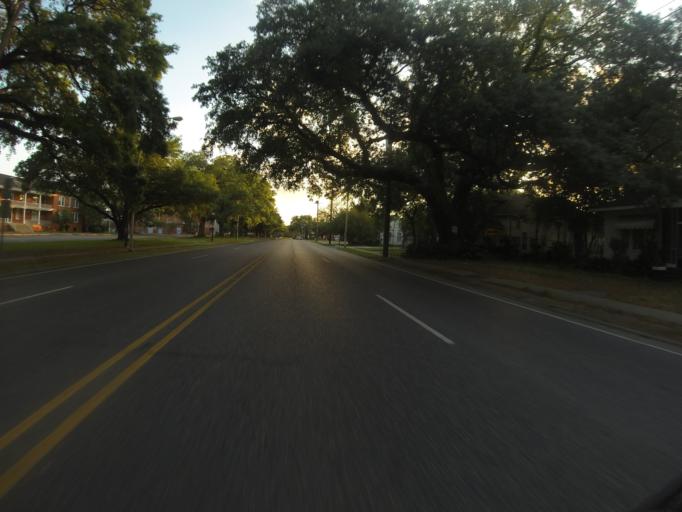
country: US
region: Louisiana
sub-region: Lafayette Parish
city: Lafayette
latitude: 30.2167
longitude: -92.0196
